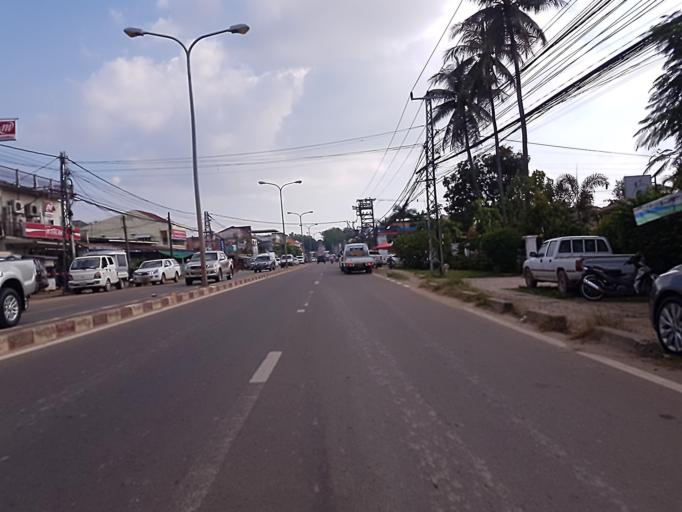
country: TH
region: Nong Khai
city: Si Chiang Mai
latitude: 17.9135
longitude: 102.6201
